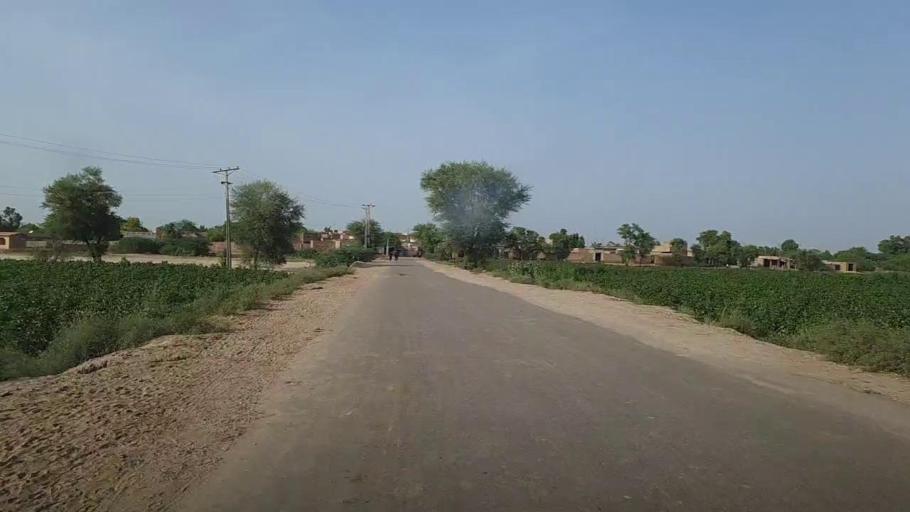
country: PK
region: Sindh
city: Ubauro
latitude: 28.1164
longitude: 69.8542
